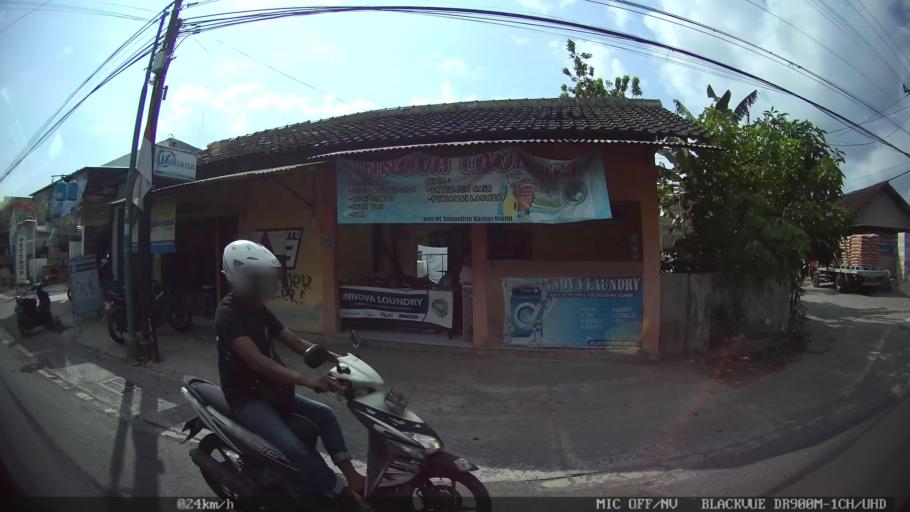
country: ID
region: Daerah Istimewa Yogyakarta
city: Kasihan
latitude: -7.8273
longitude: 110.3255
